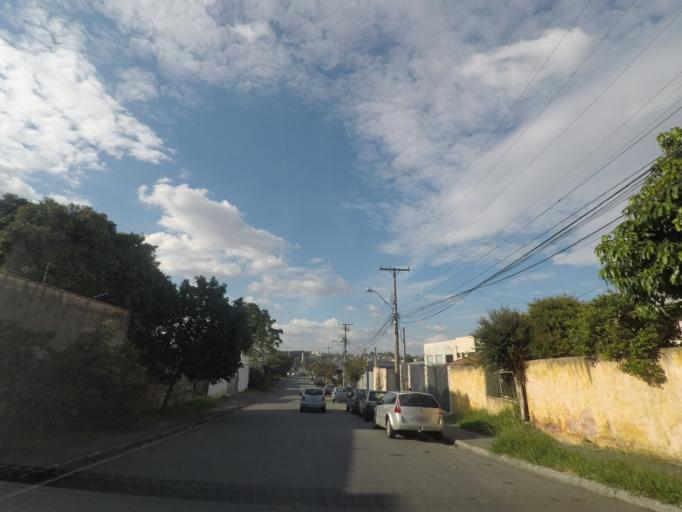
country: BR
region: Parana
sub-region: Sao Jose Dos Pinhais
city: Sao Jose dos Pinhais
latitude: -25.5084
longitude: -49.2810
